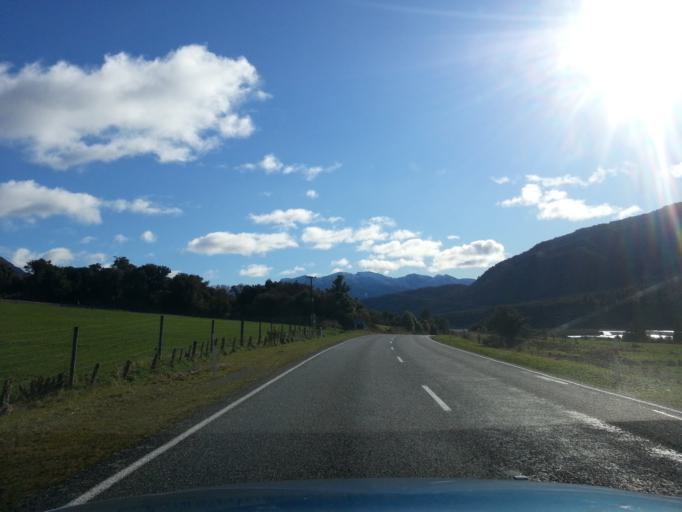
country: NZ
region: West Coast
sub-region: Grey District
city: Greymouth
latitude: -42.7463
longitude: 171.5307
